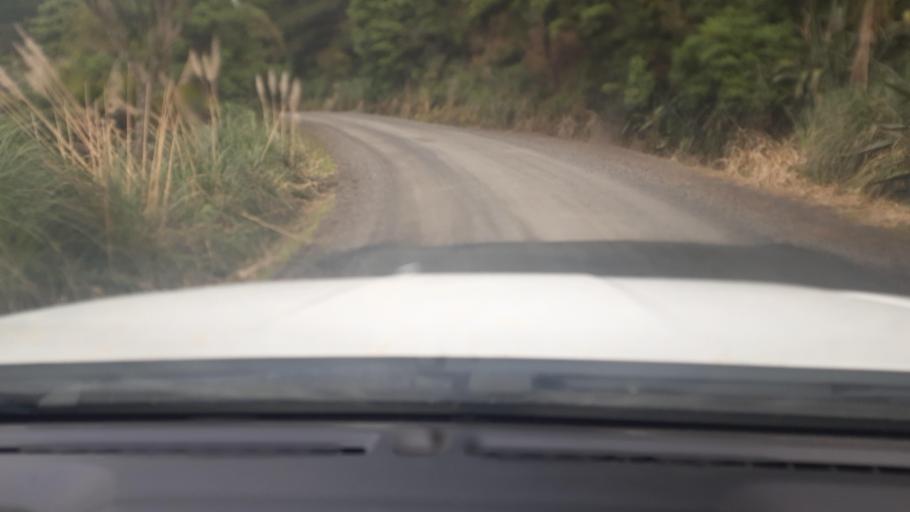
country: NZ
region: Northland
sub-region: Far North District
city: Ahipara
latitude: -35.2802
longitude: 173.2080
